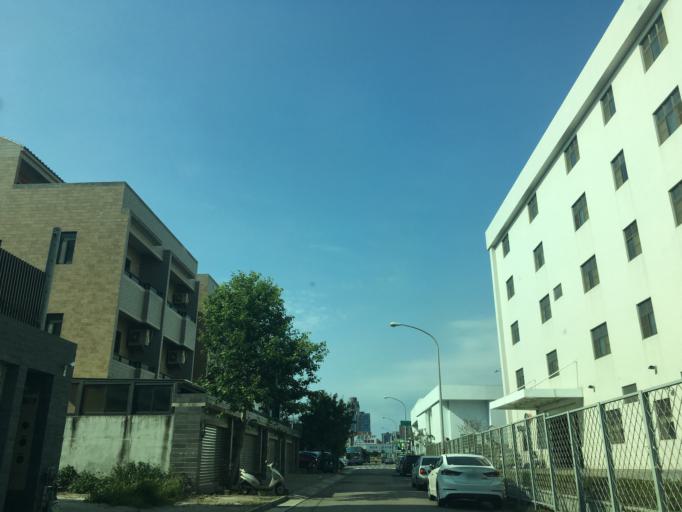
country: TW
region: Taiwan
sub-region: Taichung City
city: Taichung
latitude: 24.1583
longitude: 120.6282
